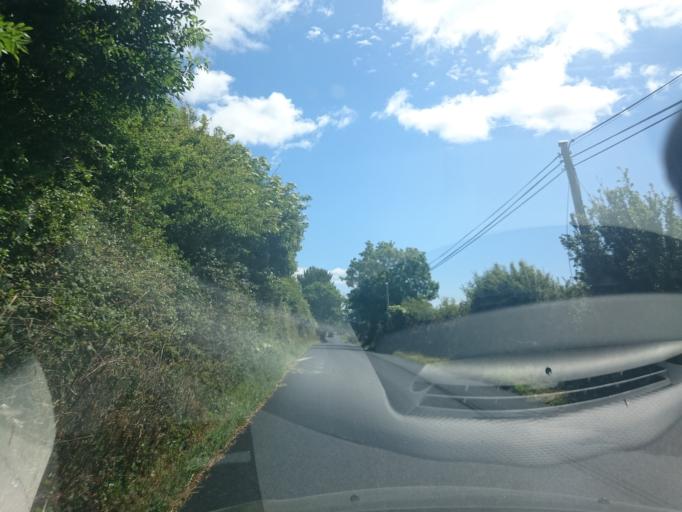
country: IE
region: Leinster
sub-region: Kilkenny
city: Thomastown
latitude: 52.6463
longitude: -7.1233
